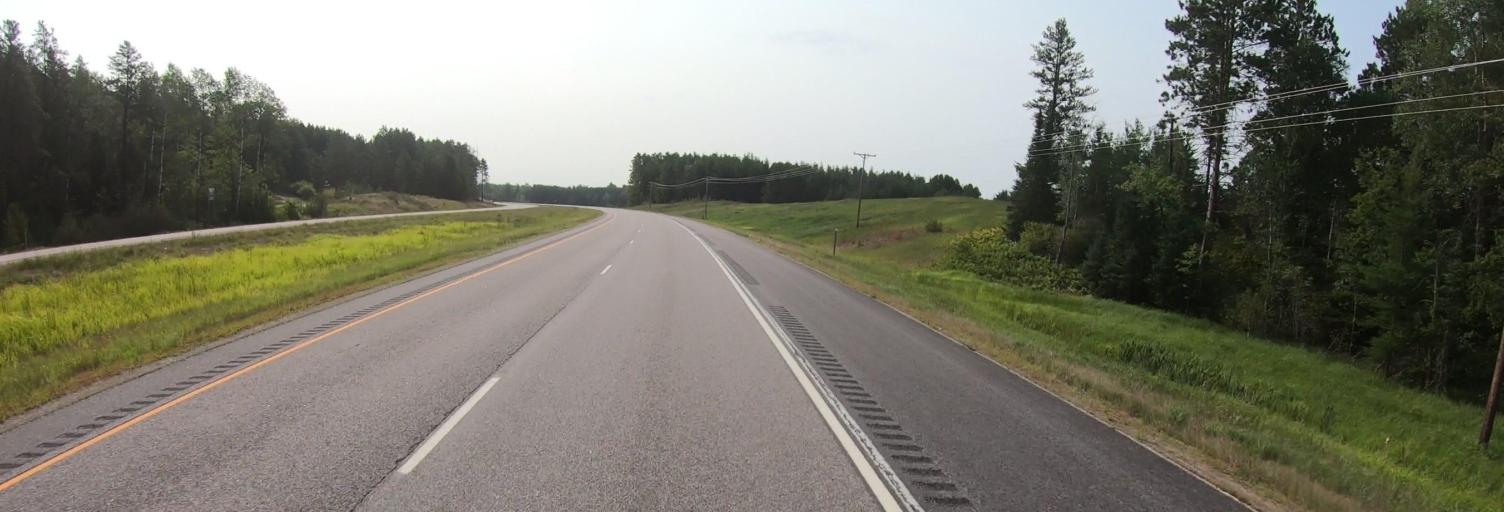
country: US
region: Minnesota
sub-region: Saint Louis County
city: Mountain Iron
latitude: 47.6699
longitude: -92.6464
